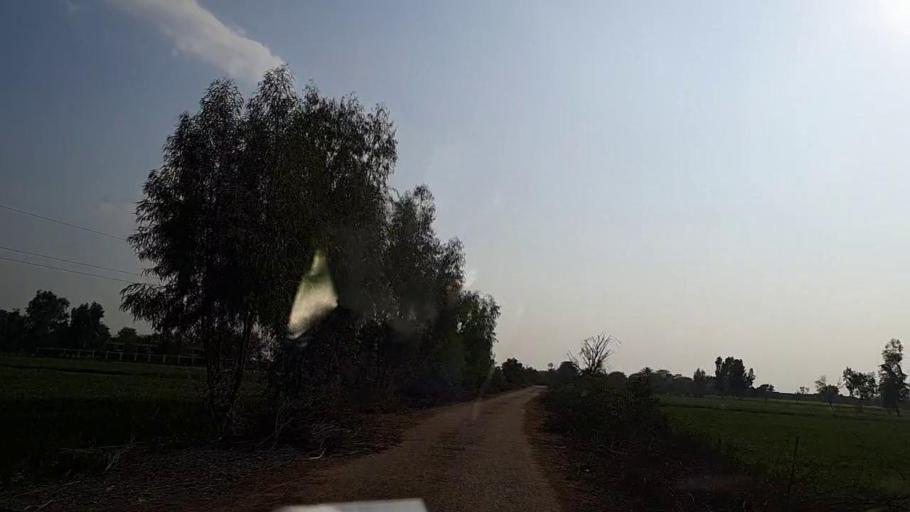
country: PK
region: Sindh
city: Nawabshah
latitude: 26.1468
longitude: 68.3903
